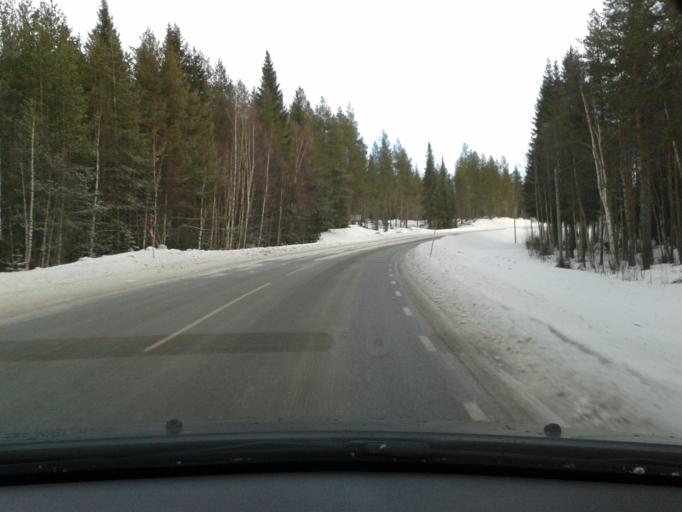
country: SE
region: Vaesterbotten
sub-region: Vilhelmina Kommun
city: Vilhelmina
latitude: 64.6477
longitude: 16.5122
